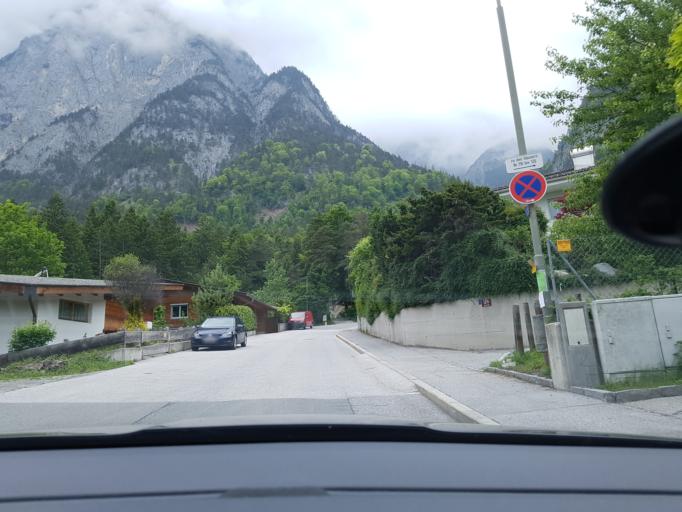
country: AT
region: Tyrol
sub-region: Politischer Bezirk Innsbruck Land
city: Vols
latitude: 47.2687
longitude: 11.3279
